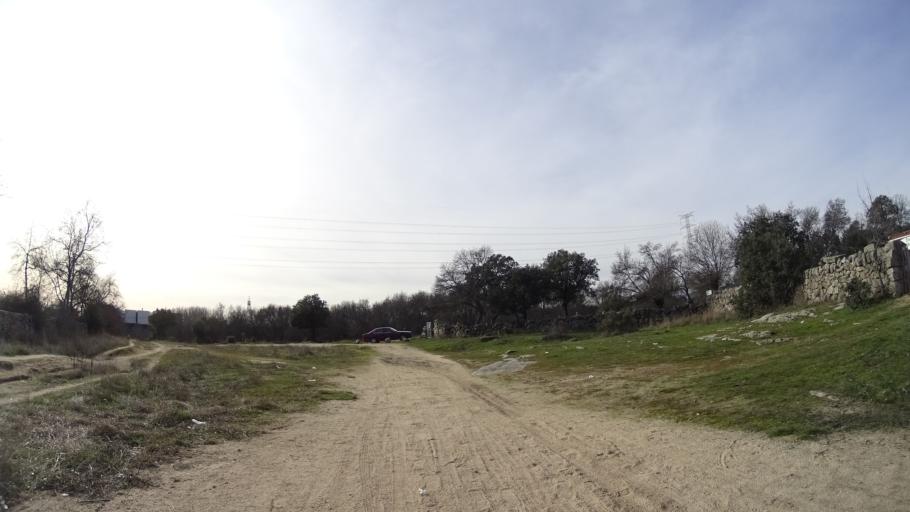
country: ES
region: Madrid
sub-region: Provincia de Madrid
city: Collado-Villalba
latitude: 40.6582
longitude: -3.9990
